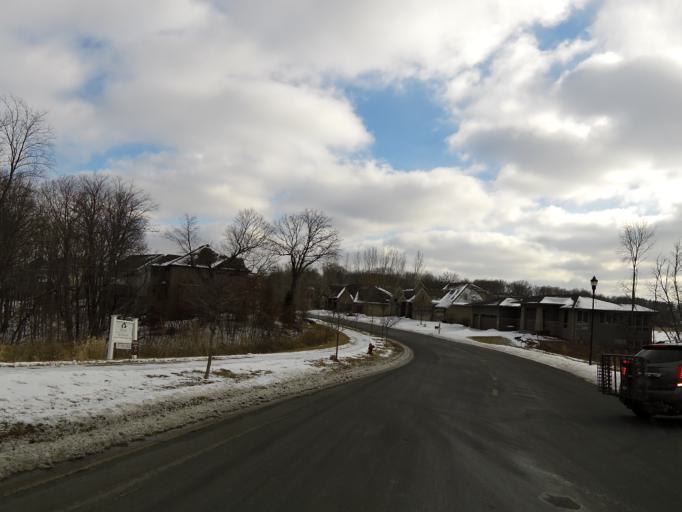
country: US
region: Minnesota
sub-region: Scott County
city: Prior Lake
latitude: 44.7338
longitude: -93.4457
